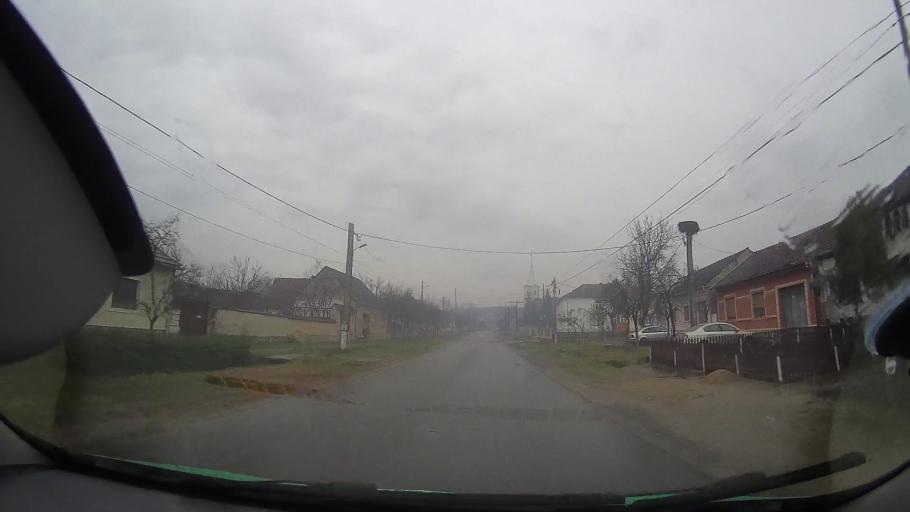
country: RO
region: Bihor
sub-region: Comuna Uileacu de Beius
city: Uileacu de Beius
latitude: 46.6842
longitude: 22.2216
